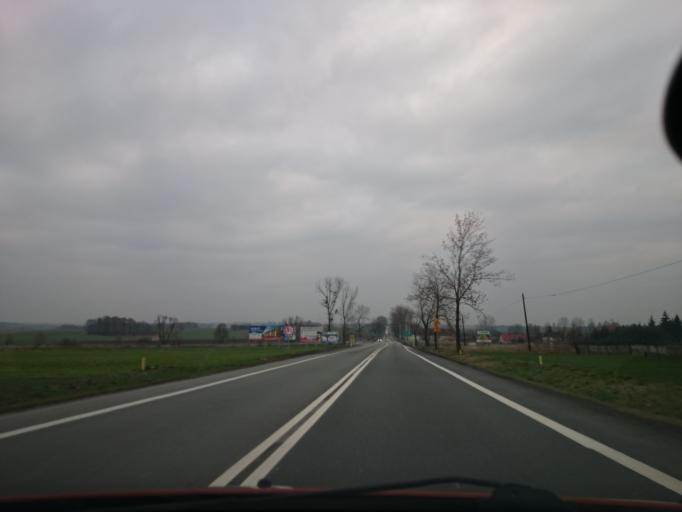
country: PL
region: Opole Voivodeship
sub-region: Powiat nyski
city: Pakoslawice
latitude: 50.5456
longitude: 17.3719
